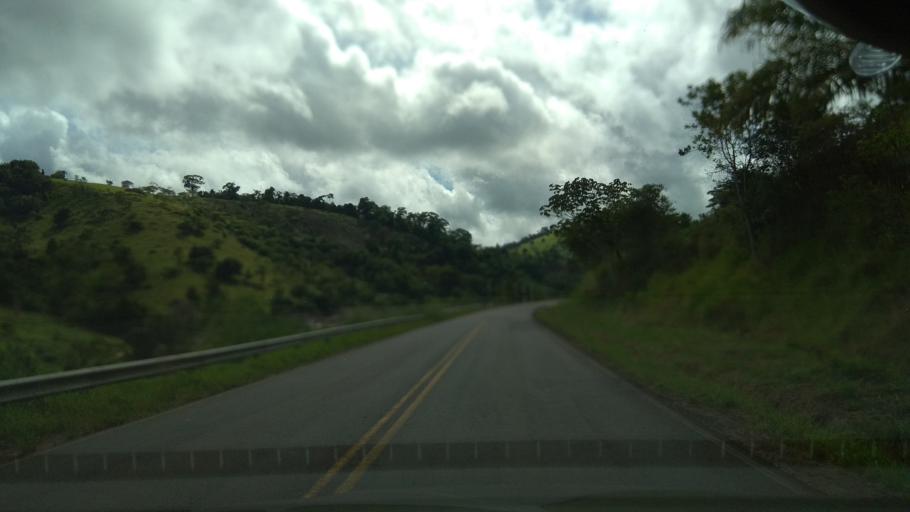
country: BR
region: Bahia
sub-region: Mutuipe
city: Mutuipe
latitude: -13.1856
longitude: -39.4413
